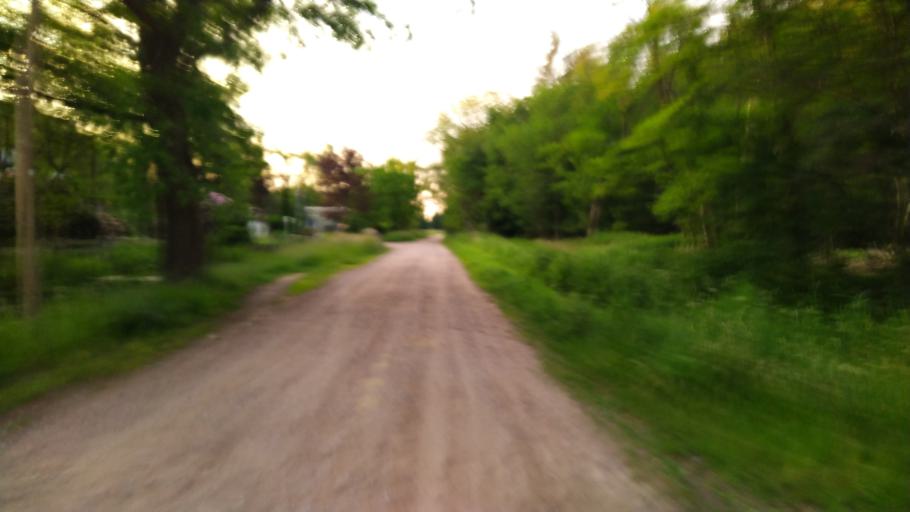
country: DE
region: Lower Saxony
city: Neu Wulmstorf
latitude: 53.4873
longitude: 9.8265
